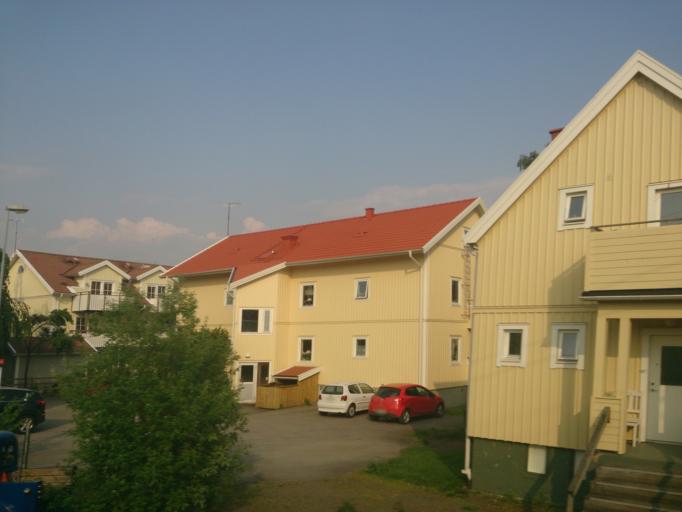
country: SE
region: Halland
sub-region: Kungsbacka Kommun
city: Kungsbacka
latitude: 57.4870
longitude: 12.0798
